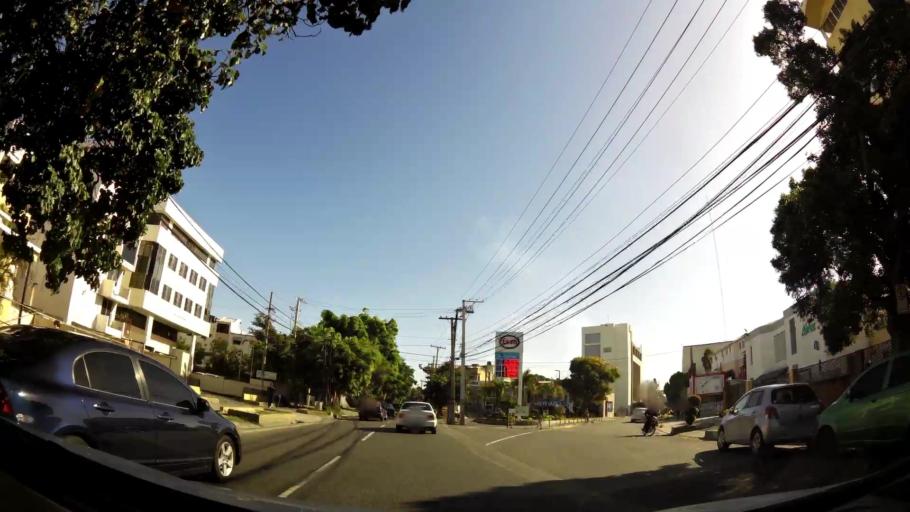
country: DO
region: Nacional
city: Ciudad Nueva
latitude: 18.4672
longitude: -69.8952
